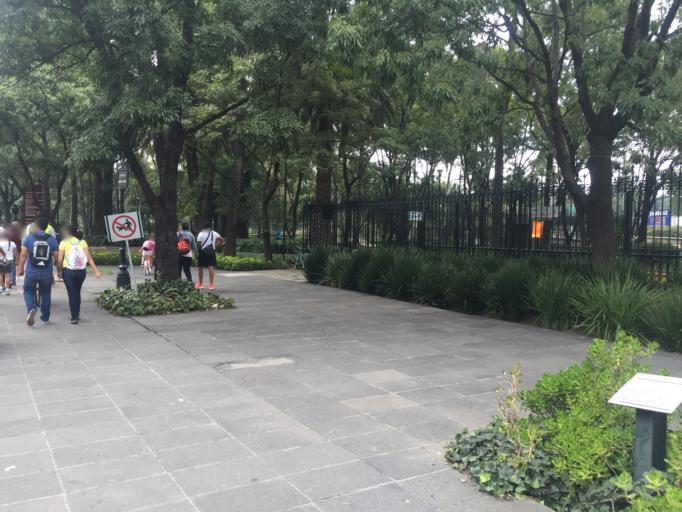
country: MX
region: Mexico City
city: Polanco
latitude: 19.4231
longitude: -99.1762
